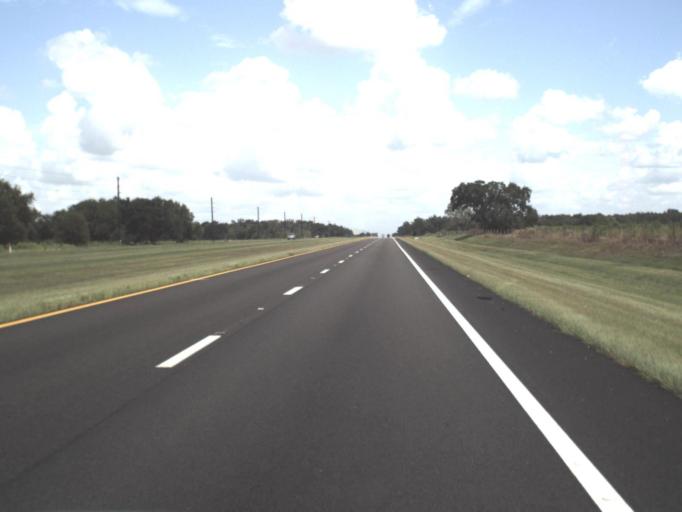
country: US
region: Florida
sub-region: Hardee County
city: Zolfo Springs
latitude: 27.4171
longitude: -81.7954
